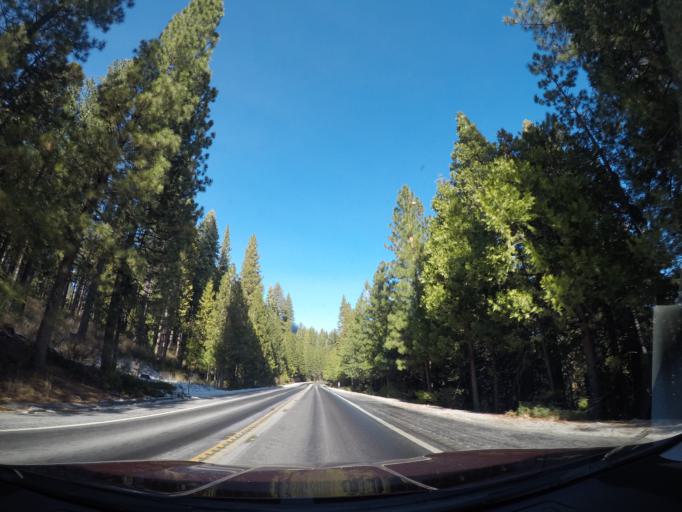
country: US
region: California
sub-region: Tuolumne County
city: Twain Harte
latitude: 38.0907
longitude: -120.1398
